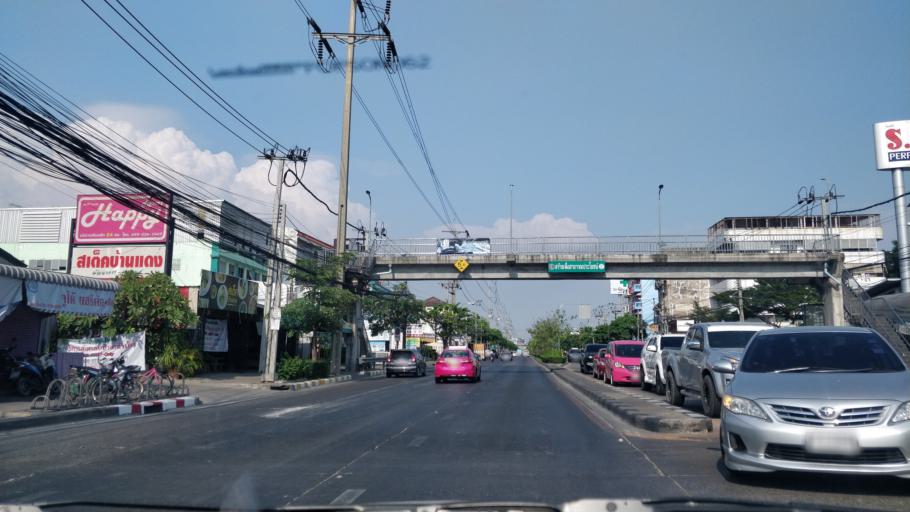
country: TH
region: Bangkok
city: Suan Luang
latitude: 13.7185
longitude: 100.6665
